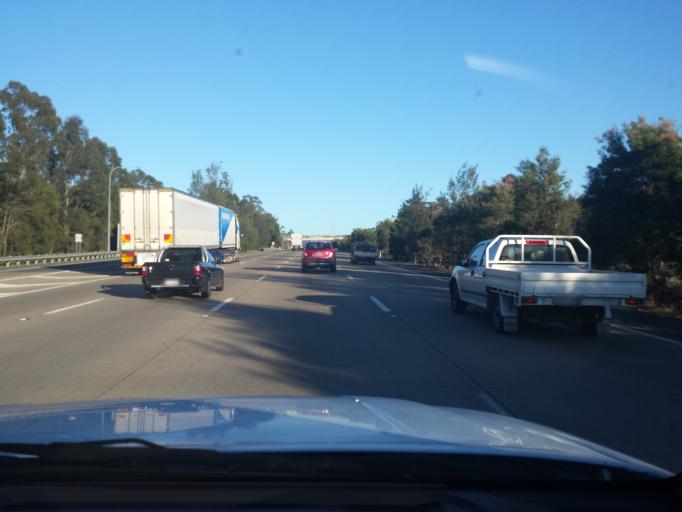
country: AU
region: Queensland
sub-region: Gold Coast
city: Ormeau Hills
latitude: -27.8224
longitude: 153.2923
